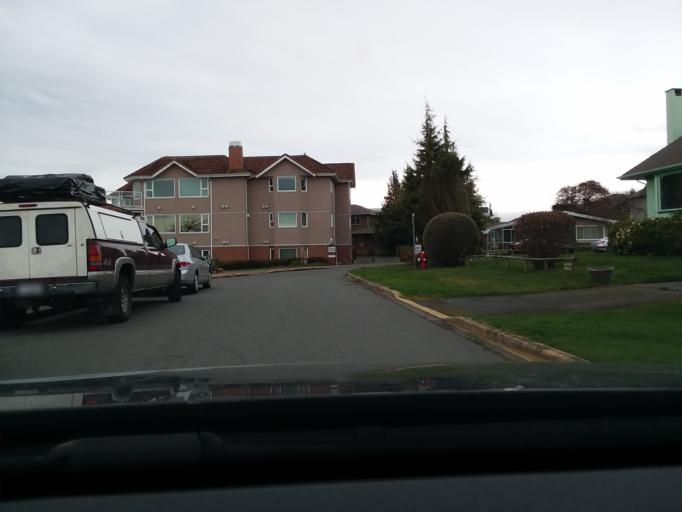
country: CA
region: British Columbia
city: North Saanich
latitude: 48.6471
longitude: -123.3941
